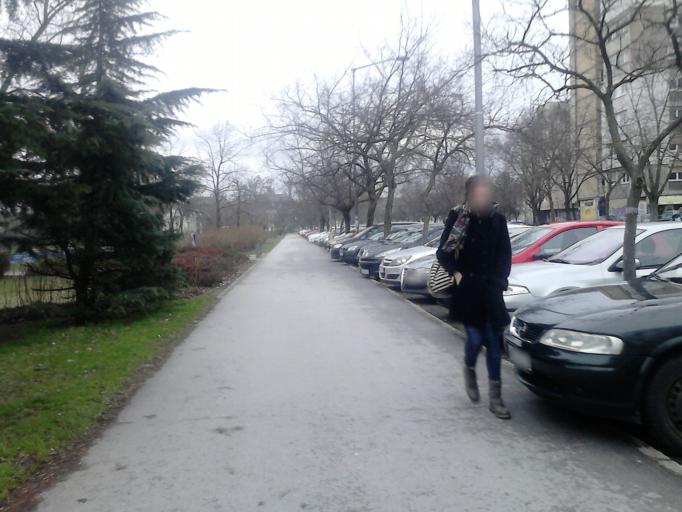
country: RS
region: Autonomna Pokrajina Vojvodina
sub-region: Juznobacki Okrug
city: Novi Sad
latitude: 45.2395
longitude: 19.8384
